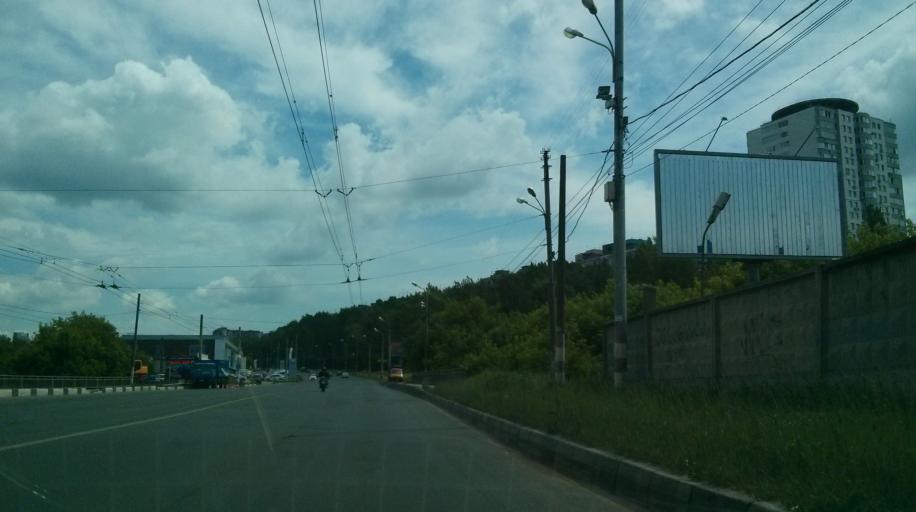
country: RU
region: Nizjnij Novgorod
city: Afonino
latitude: 56.3014
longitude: 44.0546
